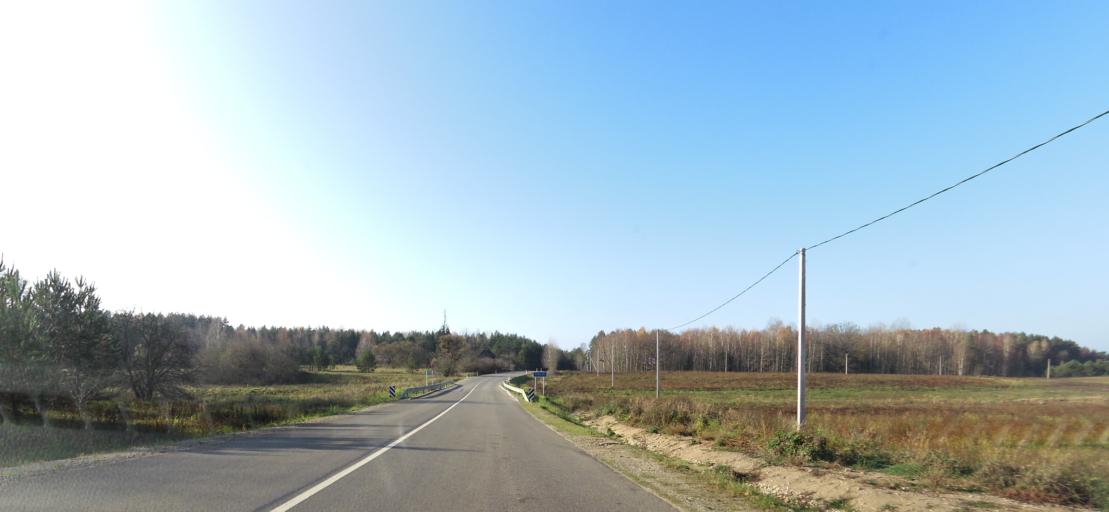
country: LT
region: Vilnius County
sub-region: Trakai
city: Rudiskes
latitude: 54.5096
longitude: 24.8762
